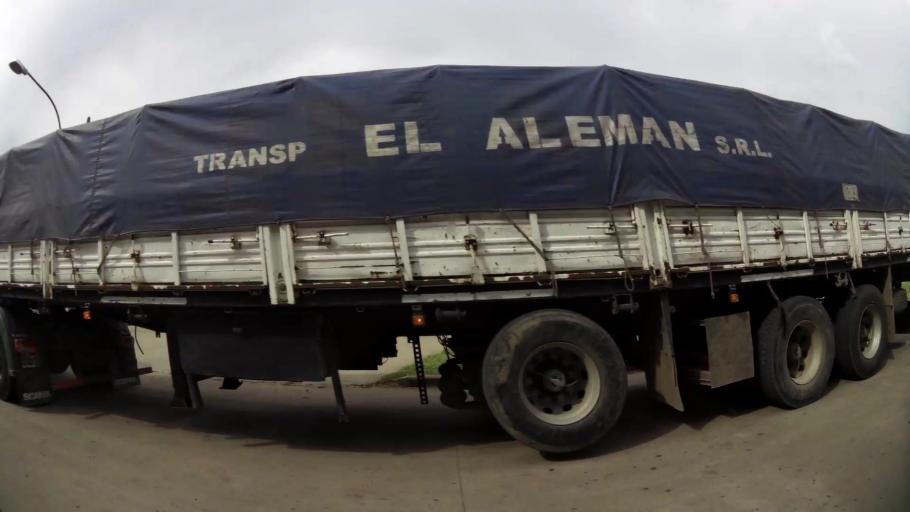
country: AR
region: Santa Fe
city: Gobernador Galvez
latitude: -33.0113
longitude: -60.6700
